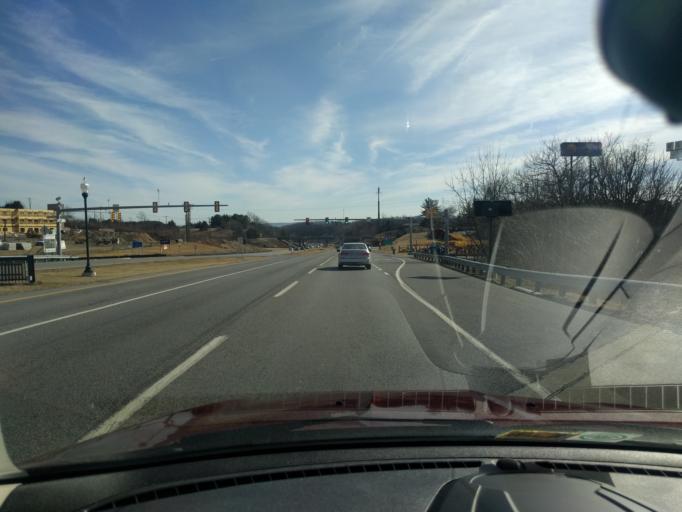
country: US
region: Virginia
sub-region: City of Staunton
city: Staunton
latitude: 38.1312
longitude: -79.0397
